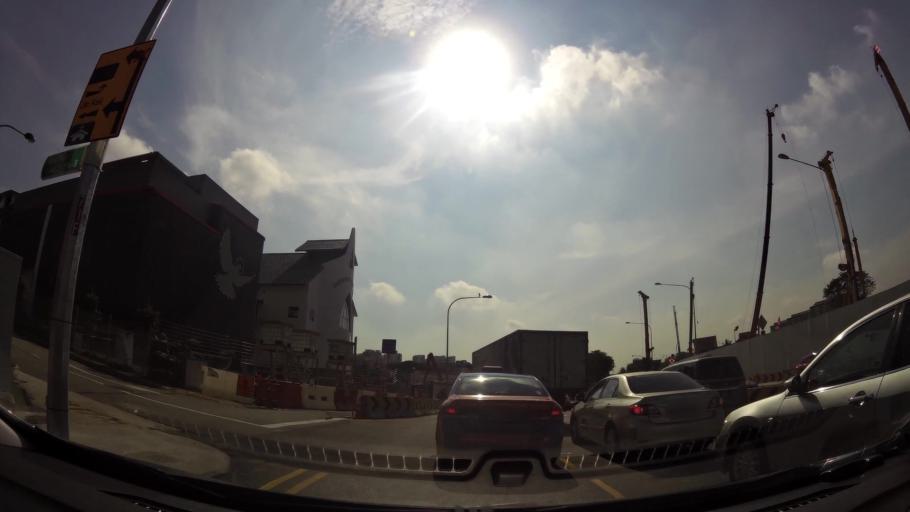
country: SG
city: Singapore
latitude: 1.3545
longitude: 103.8331
